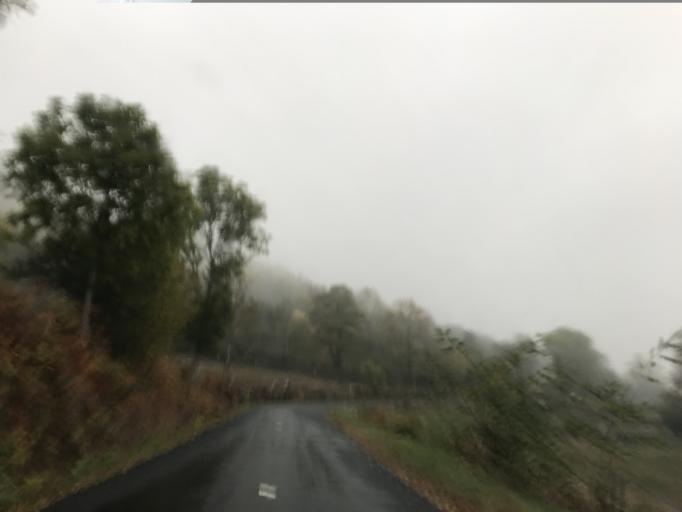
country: FR
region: Auvergne
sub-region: Departement du Puy-de-Dome
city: Celles-sur-Durolle
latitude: 45.7846
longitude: 3.6442
